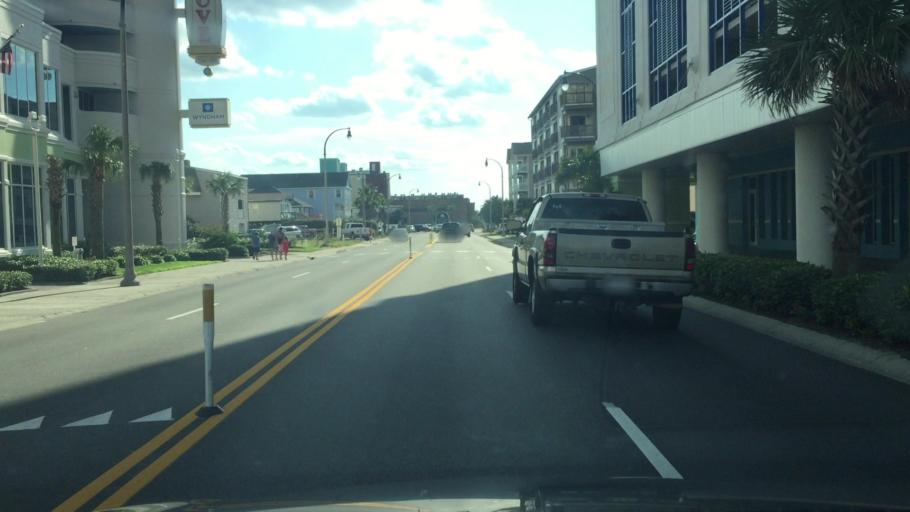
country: US
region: South Carolina
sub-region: Horry County
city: North Myrtle Beach
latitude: 33.8275
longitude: -78.6449
